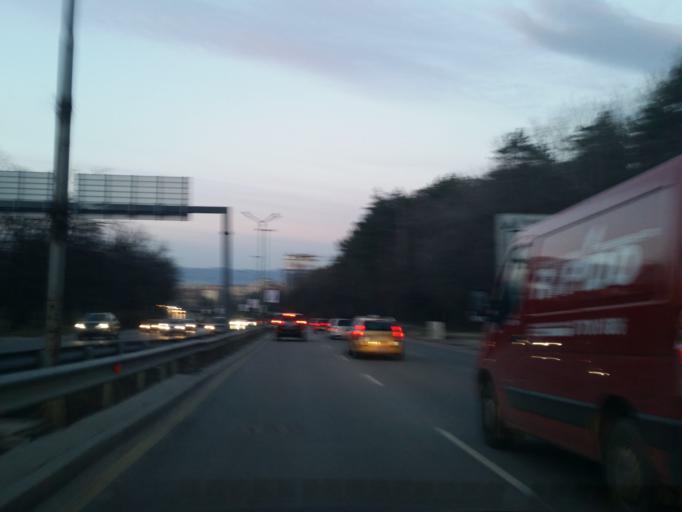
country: BG
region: Sofia-Capital
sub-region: Stolichna Obshtina
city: Sofia
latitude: 42.6793
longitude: 23.3439
